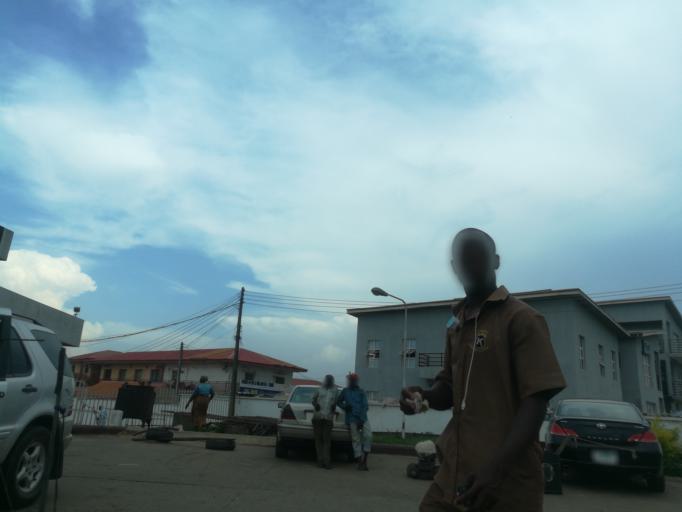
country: NG
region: Oyo
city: Ibadan
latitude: 7.4331
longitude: 3.9125
